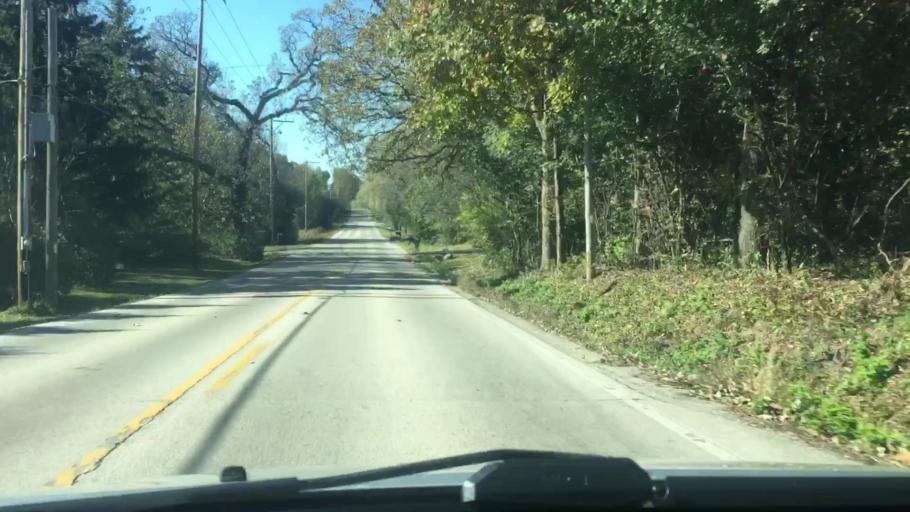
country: US
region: Wisconsin
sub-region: Waukesha County
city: Wales
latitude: 42.9881
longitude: -88.3476
